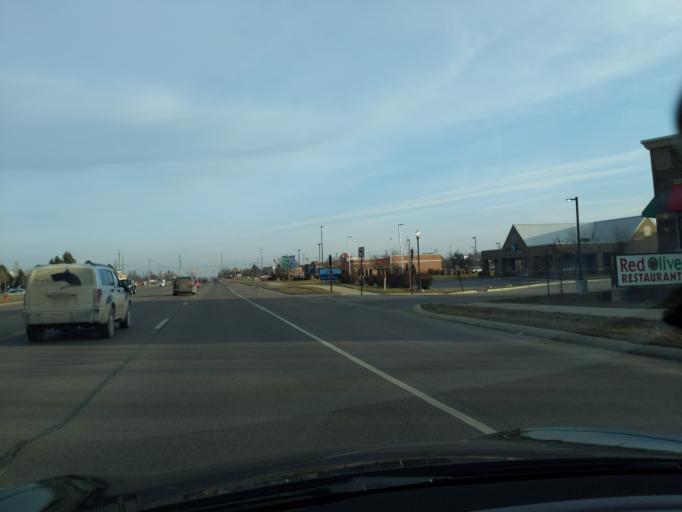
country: US
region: Michigan
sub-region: Livingston County
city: Howell
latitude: 42.5880
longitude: -83.8777
